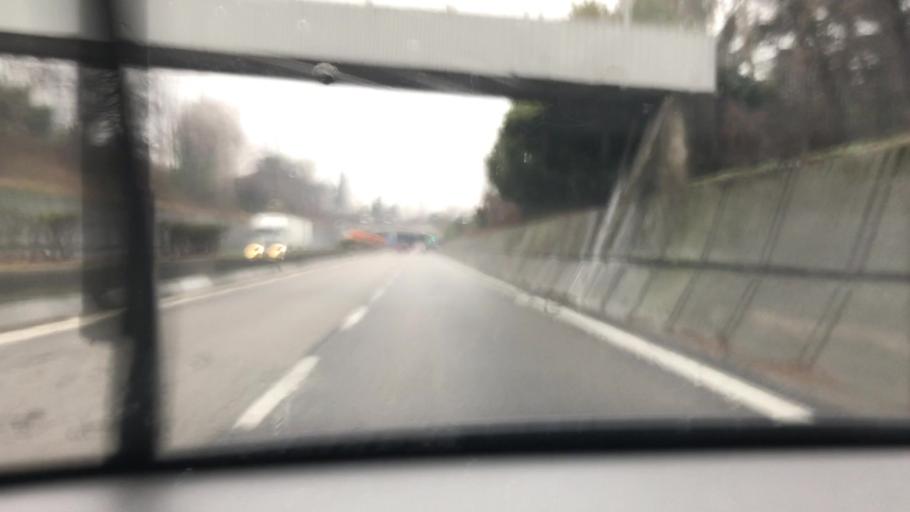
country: IT
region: Lombardy
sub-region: Provincia di Lecco
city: Colico Piano
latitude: 46.1328
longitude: 9.3823
